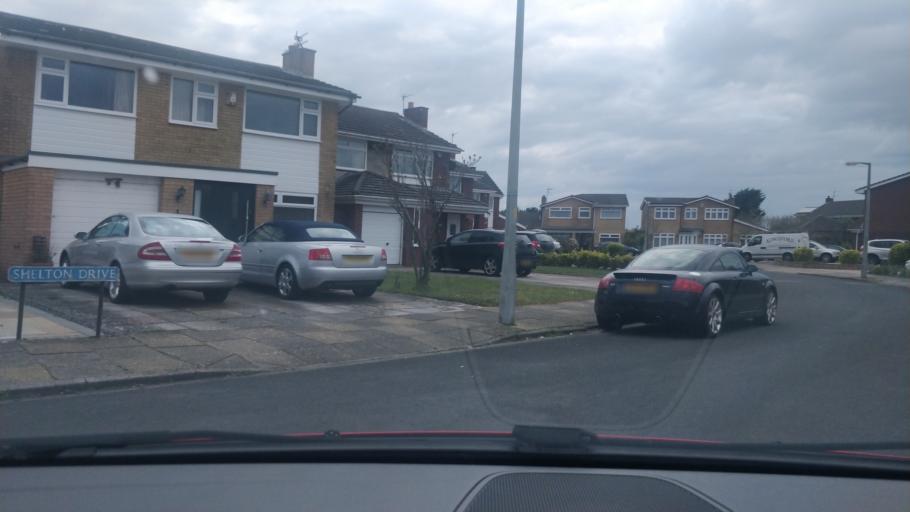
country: GB
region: England
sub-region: Sefton
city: Formby
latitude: 53.5970
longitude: -3.0531
